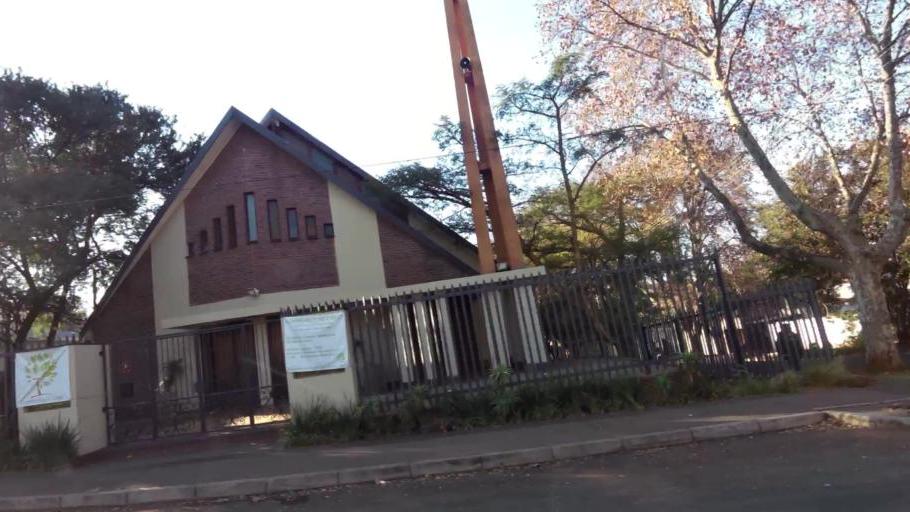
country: ZA
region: Gauteng
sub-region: City of Johannesburg Metropolitan Municipality
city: Johannesburg
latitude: -26.1746
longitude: 28.0068
